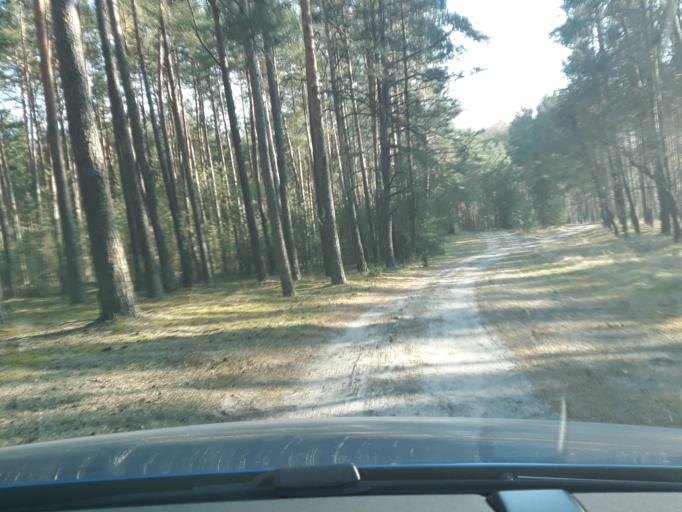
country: PL
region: Pomeranian Voivodeship
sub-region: Powiat bytowski
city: Lipnica
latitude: 53.8981
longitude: 17.4942
